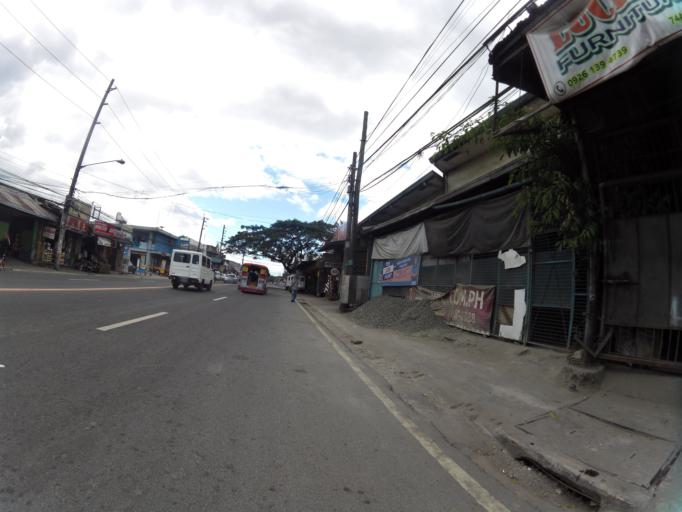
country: PH
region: Calabarzon
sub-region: Province of Rizal
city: Antipolo
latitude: 14.6305
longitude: 121.1189
